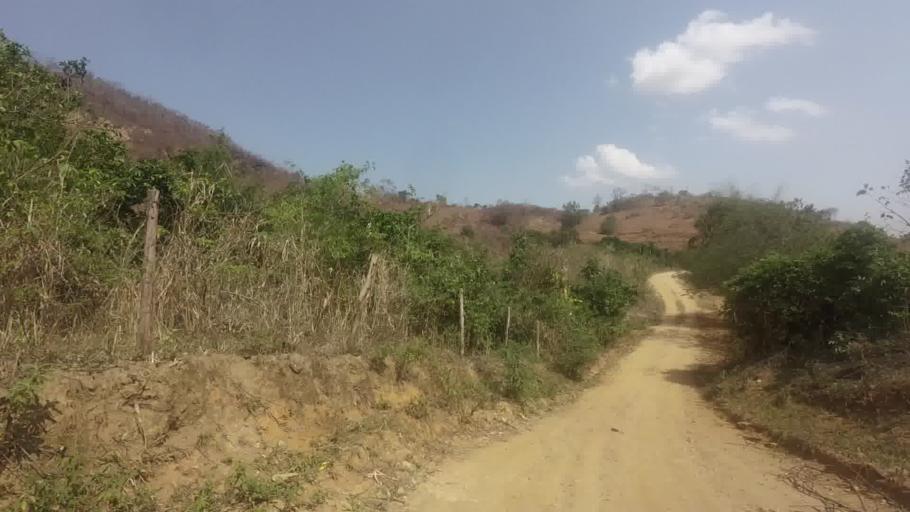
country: BR
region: Espirito Santo
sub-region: Sao Jose Do Calcado
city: Sao Jose do Calcado
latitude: -21.0194
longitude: -41.5161
